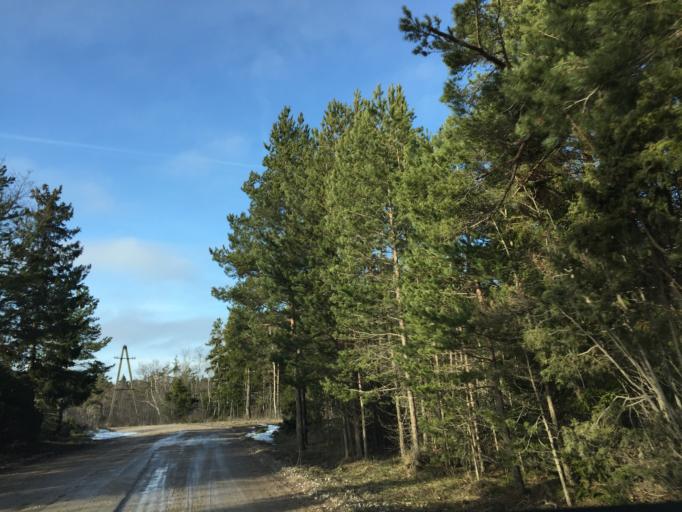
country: EE
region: Saare
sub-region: Kuressaare linn
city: Kuressaare
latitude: 58.4686
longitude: 21.9902
